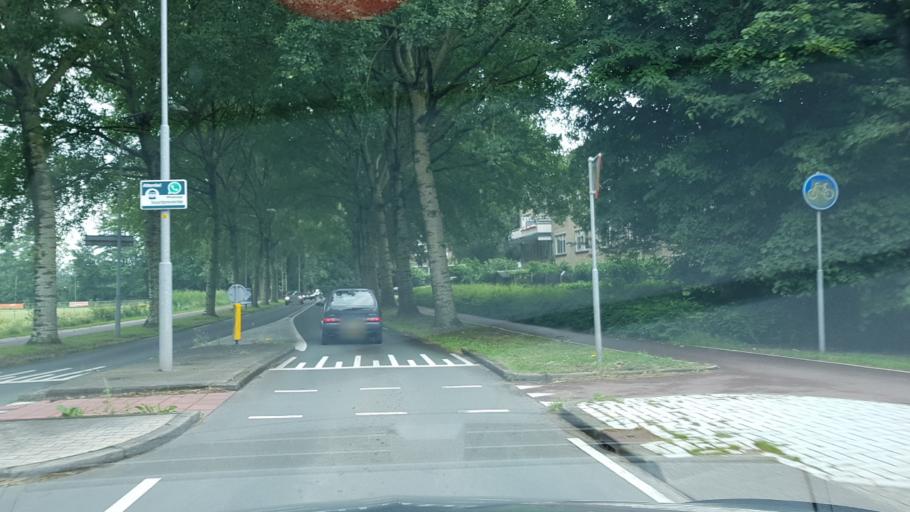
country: NL
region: North Holland
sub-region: Gemeente Velsen
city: Velsen-Zuid
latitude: 52.4422
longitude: 4.6595
